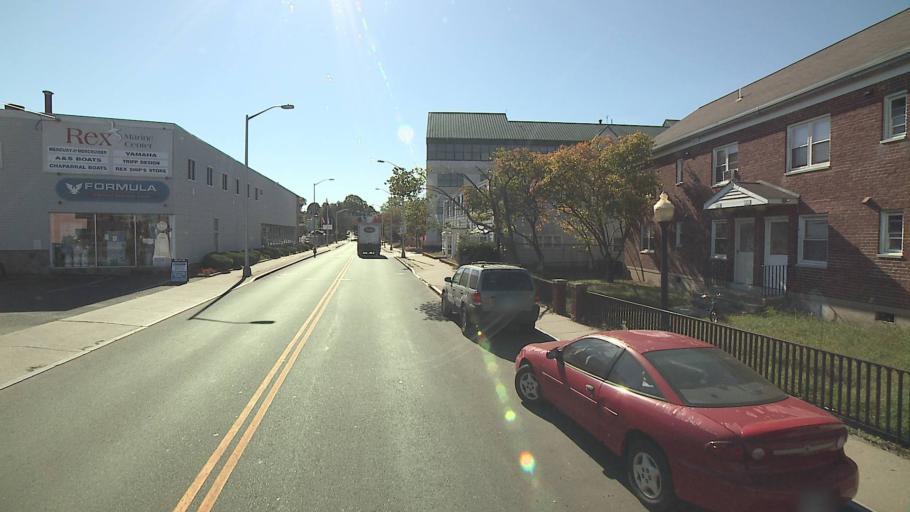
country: US
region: Connecticut
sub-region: Fairfield County
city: East Norwalk
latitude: 41.0939
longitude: -73.4153
